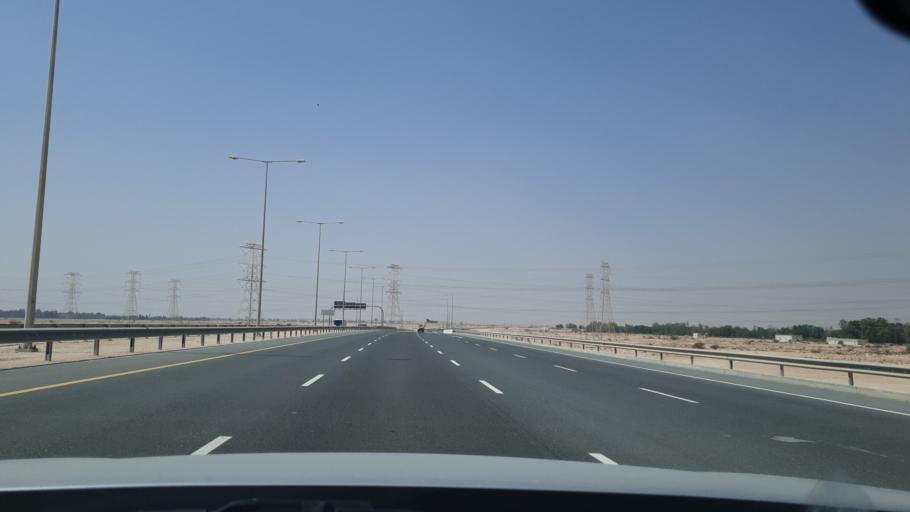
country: QA
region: Baladiyat az Za`ayin
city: Az Za`ayin
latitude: 25.6176
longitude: 51.3612
